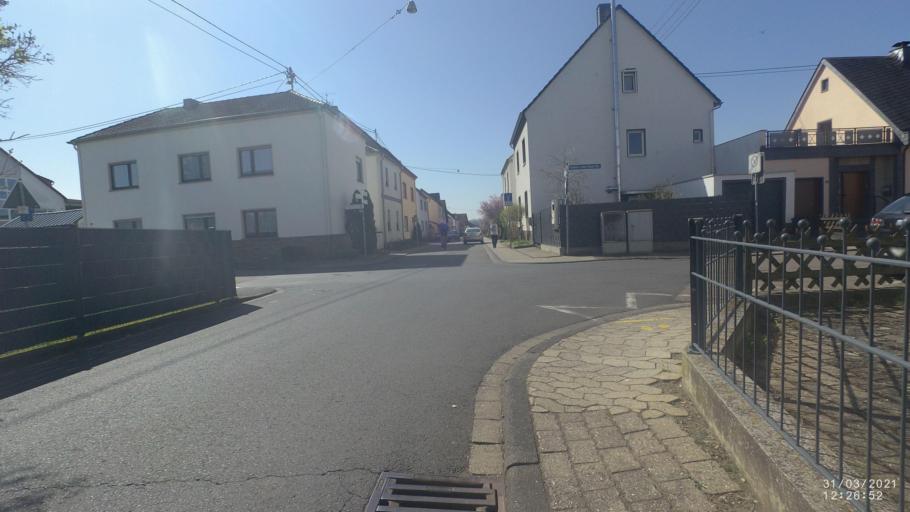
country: DE
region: Rheinland-Pfalz
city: Sankt Sebastian
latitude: 50.4107
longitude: 7.5625
